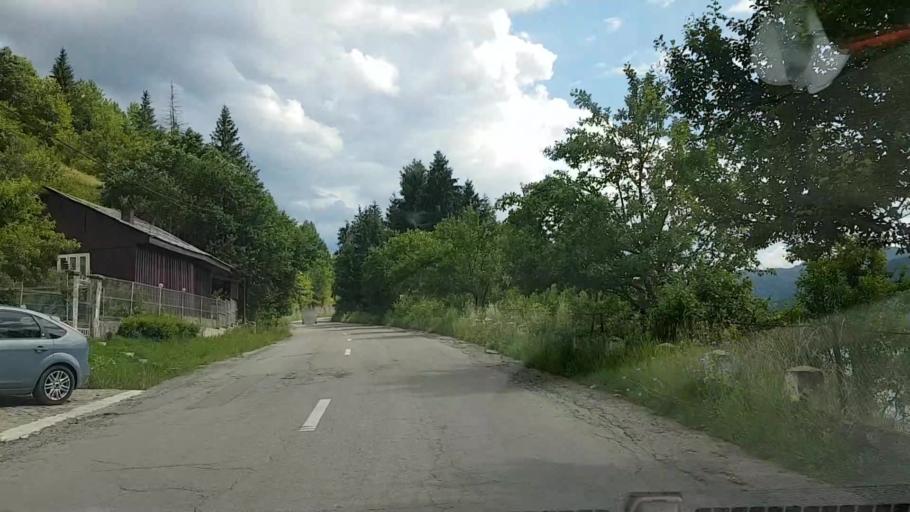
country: RO
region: Neamt
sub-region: Comuna Hangu
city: Hangu
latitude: 47.0557
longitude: 26.0376
